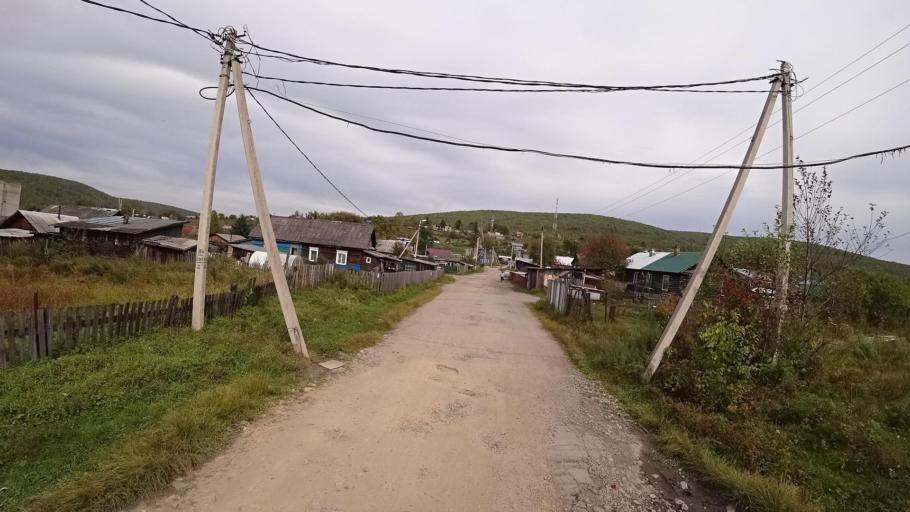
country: RU
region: Jewish Autonomous Oblast
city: Khingansk
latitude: 49.1254
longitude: 131.1990
